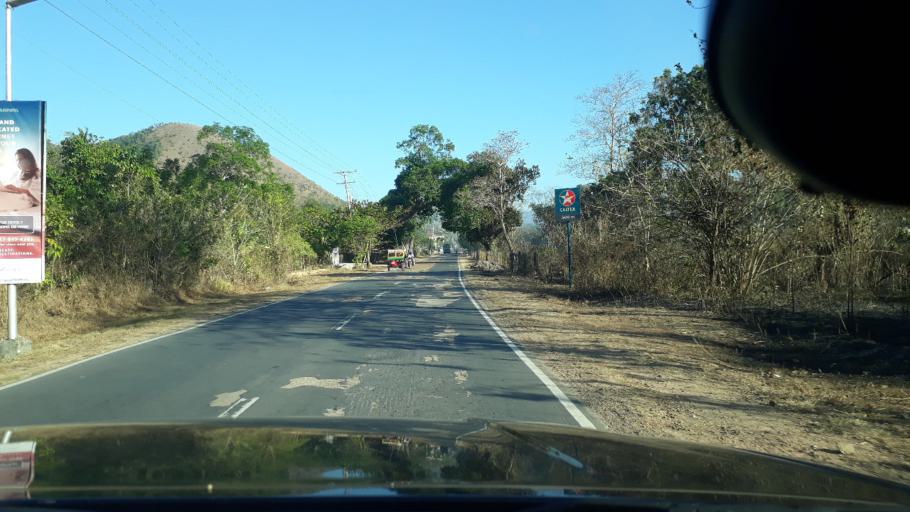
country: PH
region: Mimaropa
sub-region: Province of Palawan
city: Coron
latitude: 12.0299
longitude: 120.1754
